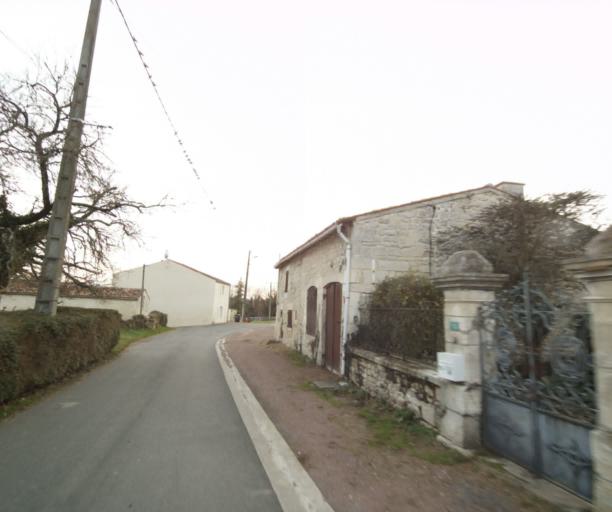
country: FR
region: Poitou-Charentes
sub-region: Departement de la Charente-Maritime
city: Fontcouverte
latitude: 45.7729
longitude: -0.5950
